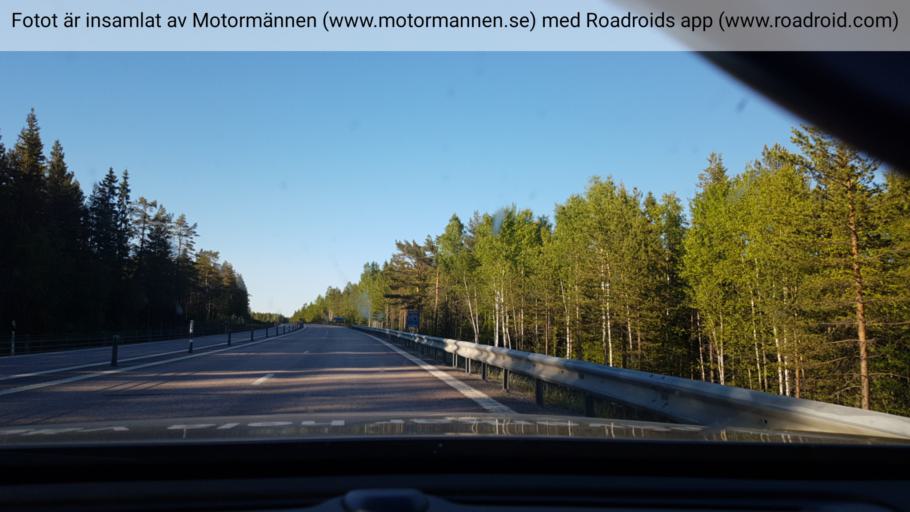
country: SE
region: Vaesternorrland
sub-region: OErnskoeldsviks Kommun
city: Husum
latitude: 63.4726
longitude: 19.2843
